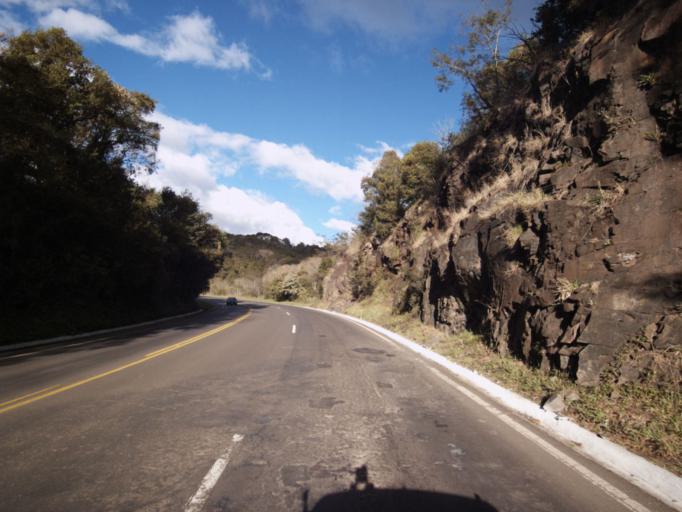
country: BR
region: Santa Catarina
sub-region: Joacaba
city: Joacaba
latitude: -27.2952
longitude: -51.4091
